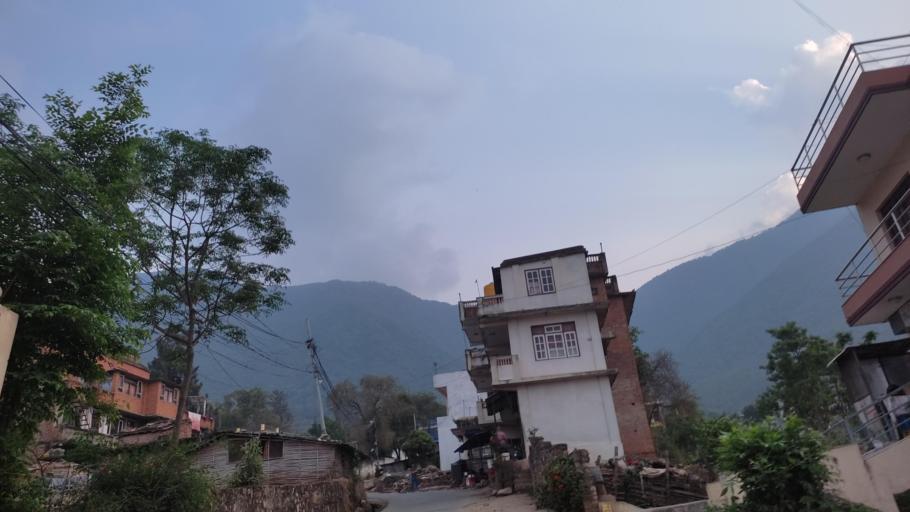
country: NP
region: Central Region
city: Kirtipur
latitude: 27.6630
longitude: 85.2542
